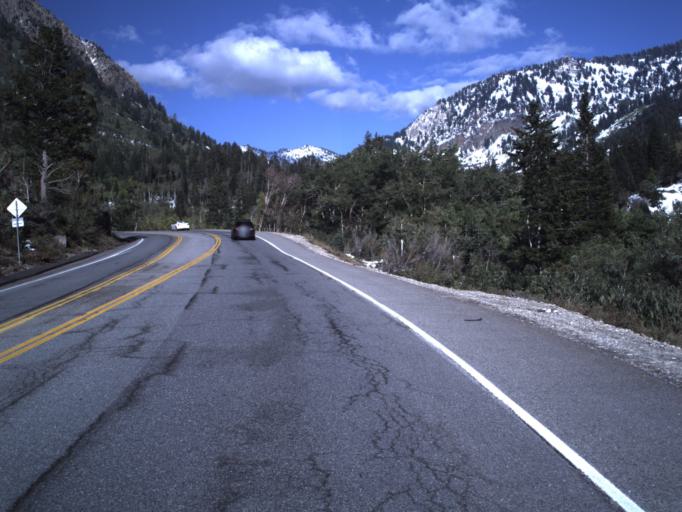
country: US
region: Utah
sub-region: Salt Lake County
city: Granite
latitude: 40.5763
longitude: -111.6783
